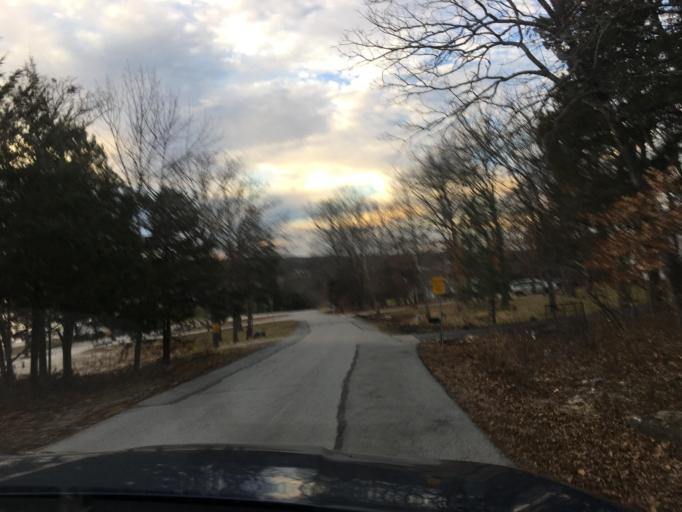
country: US
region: Missouri
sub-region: Jefferson County
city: De Soto
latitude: 38.0953
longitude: -90.5674
